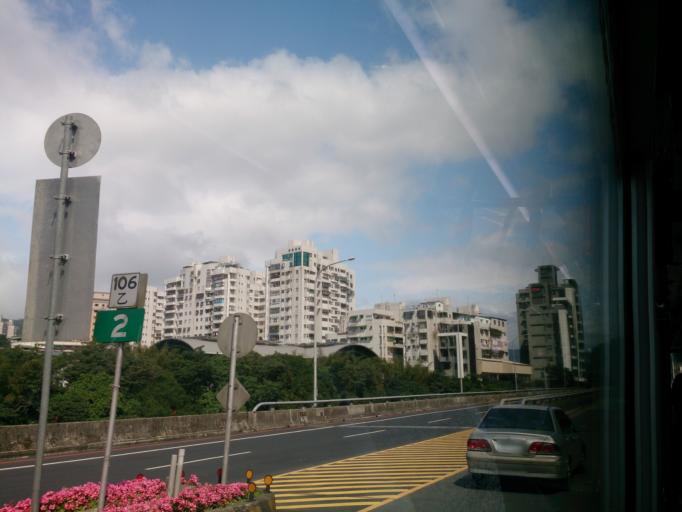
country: TW
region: Taipei
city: Taipei
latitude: 24.9993
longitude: 121.6177
